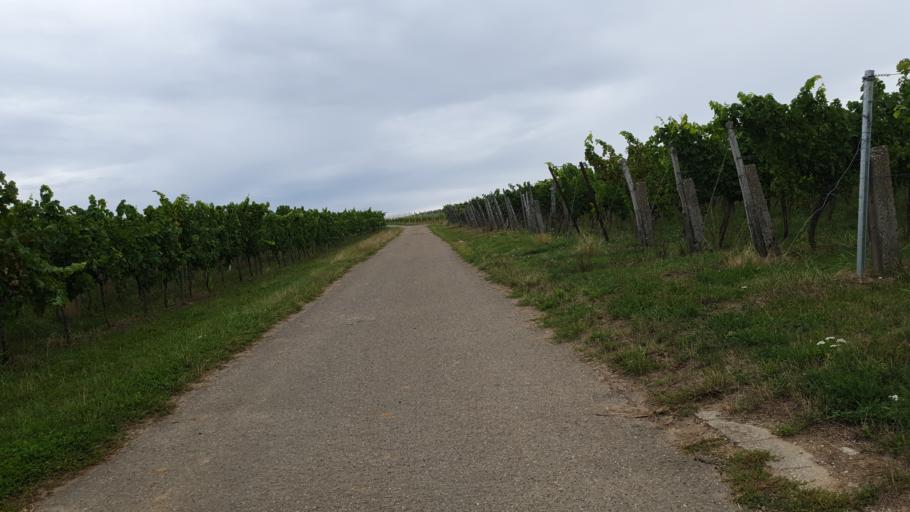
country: DE
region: Rheinland-Pfalz
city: Niederhorbach
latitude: 49.1090
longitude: 8.0397
